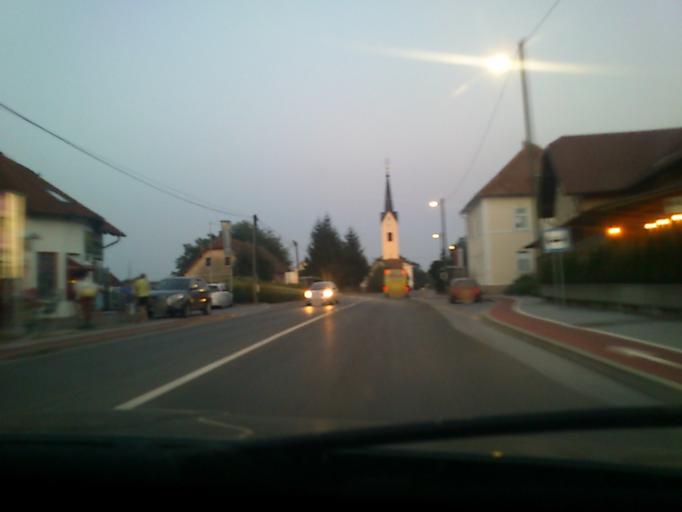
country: SI
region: Starse
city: Starse
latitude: 46.4671
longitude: 15.7651
